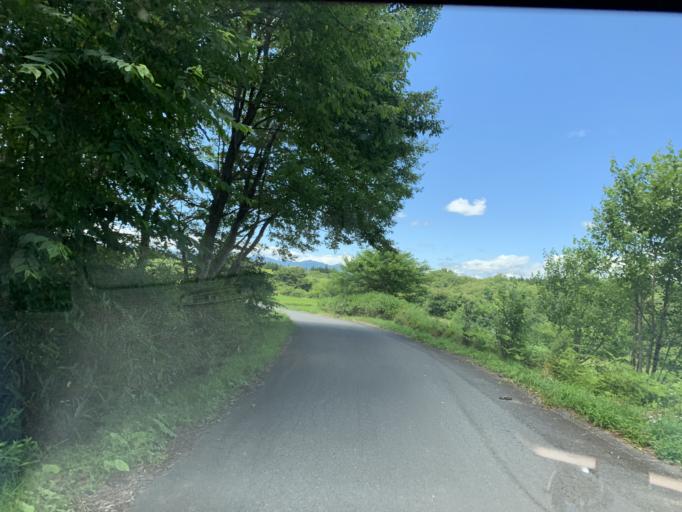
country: JP
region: Iwate
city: Ichinoseki
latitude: 38.9299
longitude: 141.0417
